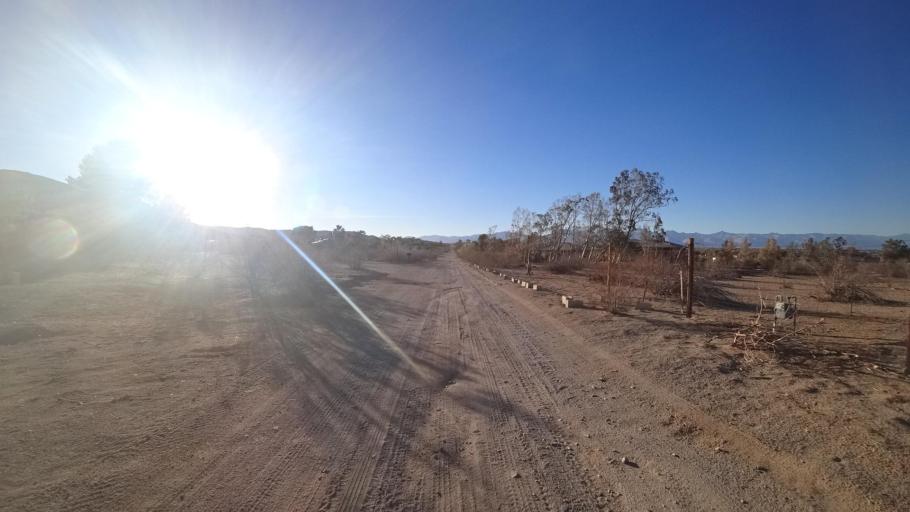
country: US
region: California
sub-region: Kern County
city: Ridgecrest
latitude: 35.5824
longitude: -117.6535
